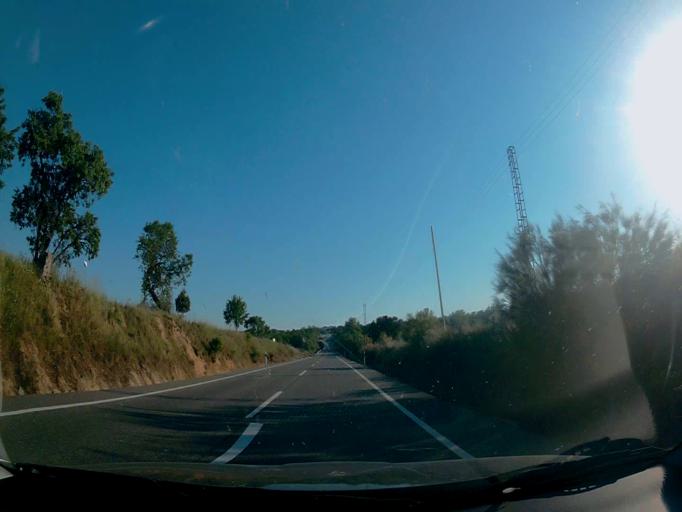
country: ES
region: Castille-La Mancha
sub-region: Province of Toledo
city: Escalona
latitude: 40.1947
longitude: -4.4013
